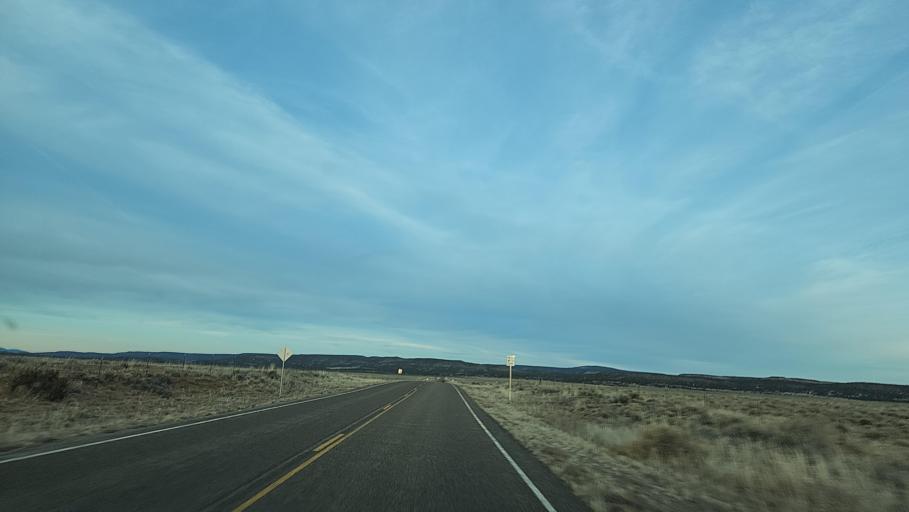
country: US
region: New Mexico
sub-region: Cibola County
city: Grants
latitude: 34.7033
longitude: -108.0258
